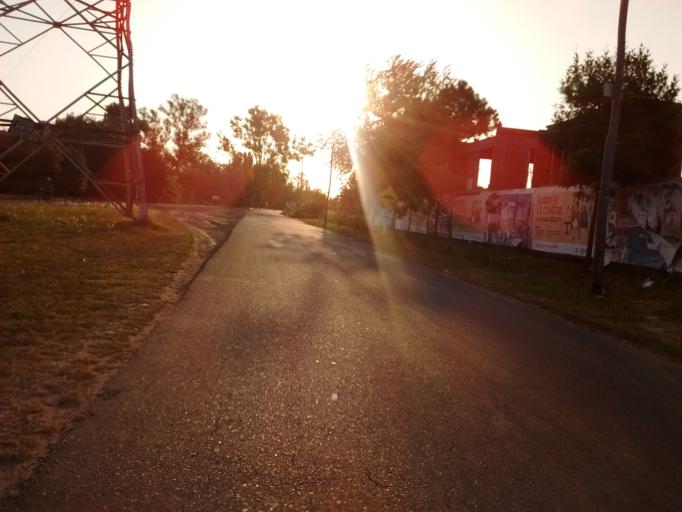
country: AR
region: Santa Fe
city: Funes
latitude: -32.9185
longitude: -60.7634
